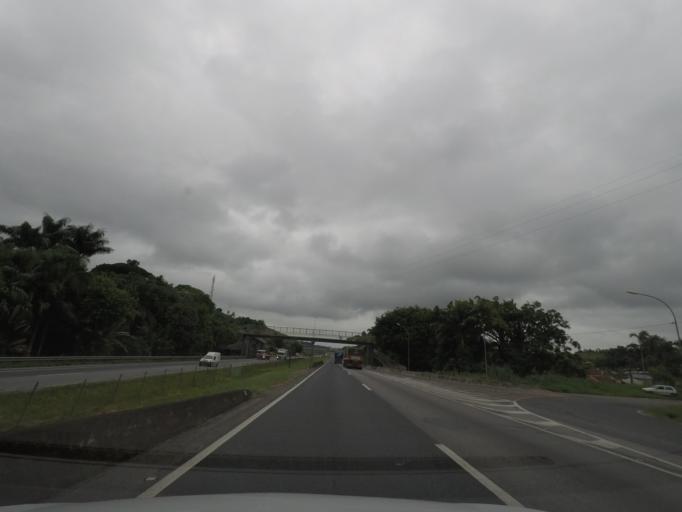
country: BR
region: Sao Paulo
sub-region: Registro
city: Registro
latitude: -24.4052
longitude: -47.7427
